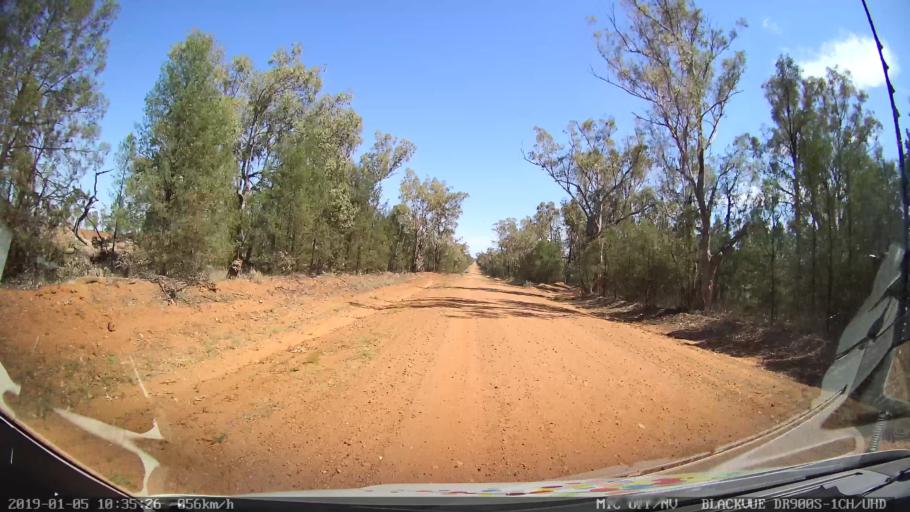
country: AU
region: New South Wales
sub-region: Gilgandra
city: Gilgandra
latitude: -31.4903
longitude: 148.9289
